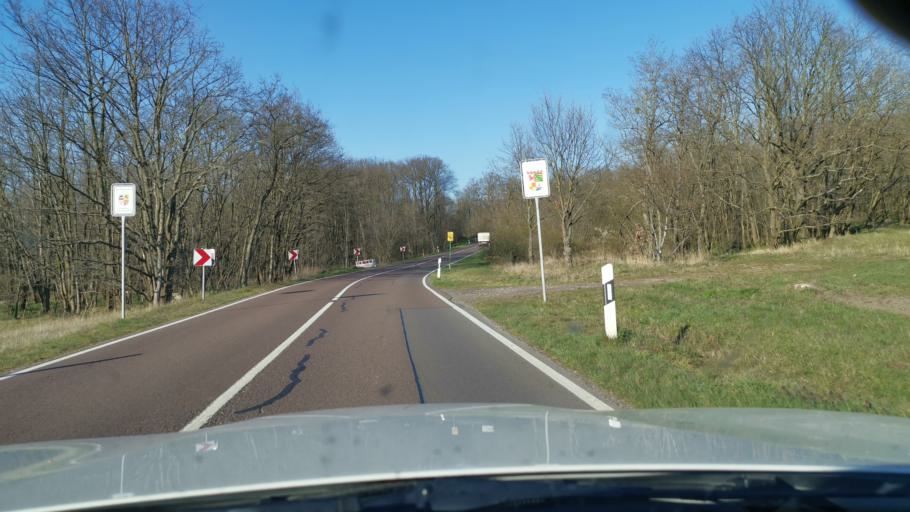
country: DE
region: Saxony-Anhalt
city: Mohlau
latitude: 51.7333
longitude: 12.3219
